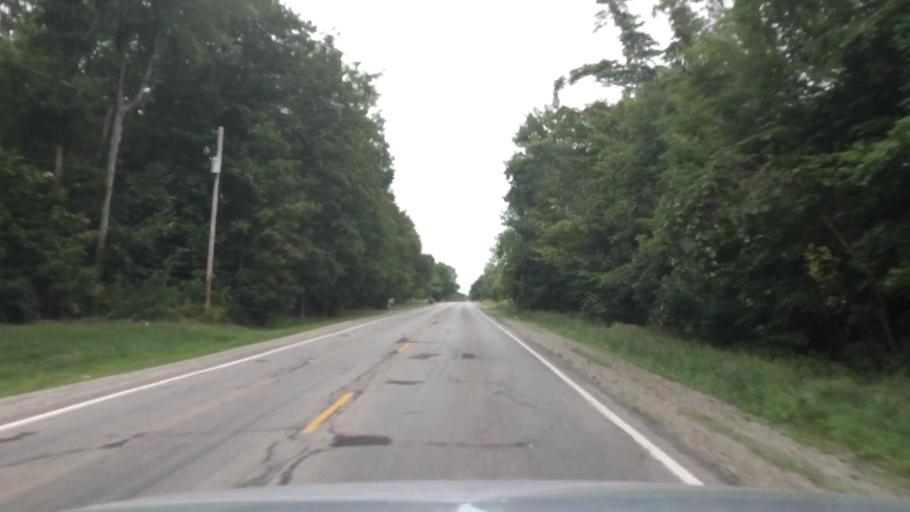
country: US
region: Michigan
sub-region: Genesee County
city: Lake Fenton
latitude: 42.8856
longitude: -83.7090
